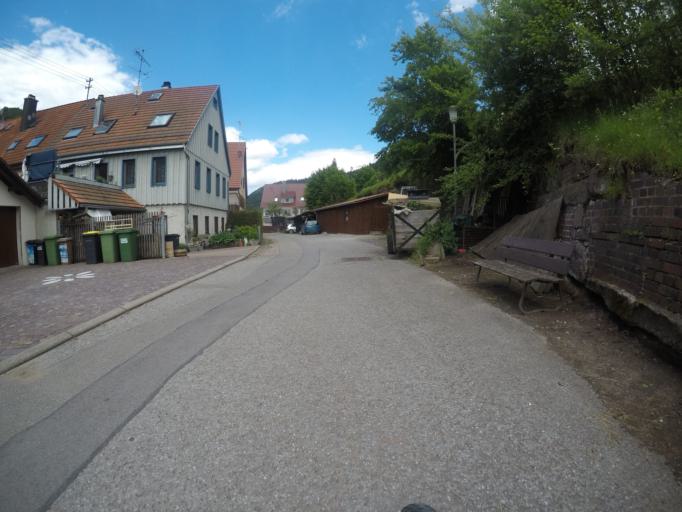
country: DE
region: Baden-Wuerttemberg
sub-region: Karlsruhe Region
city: Bad Liebenzell
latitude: 48.7481
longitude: 8.7327
